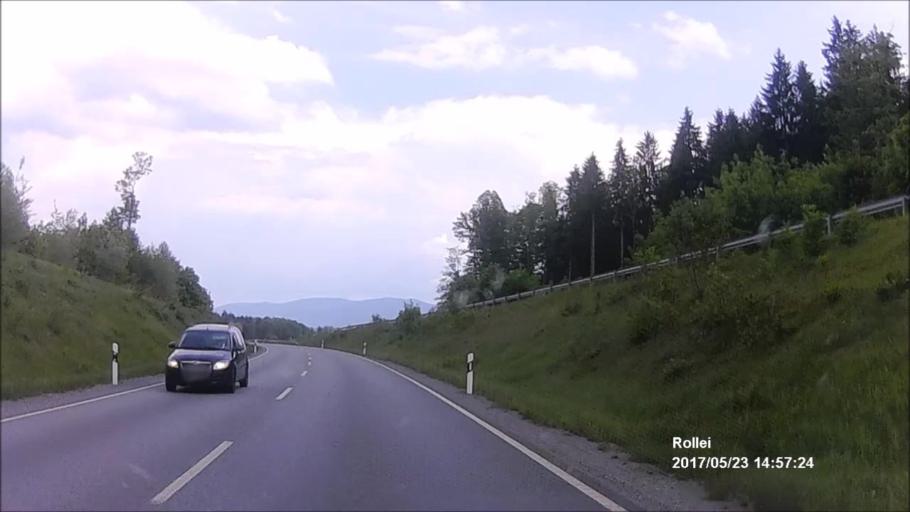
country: DE
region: Bavaria
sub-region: Upper Bavaria
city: Traunstein
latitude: 47.8854
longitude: 12.6492
